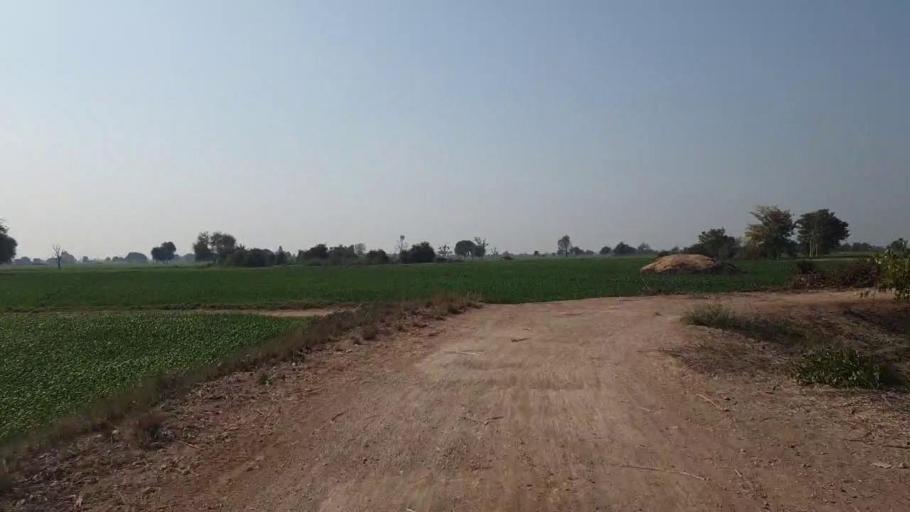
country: PK
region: Sindh
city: Hala
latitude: 25.9225
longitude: 68.4098
